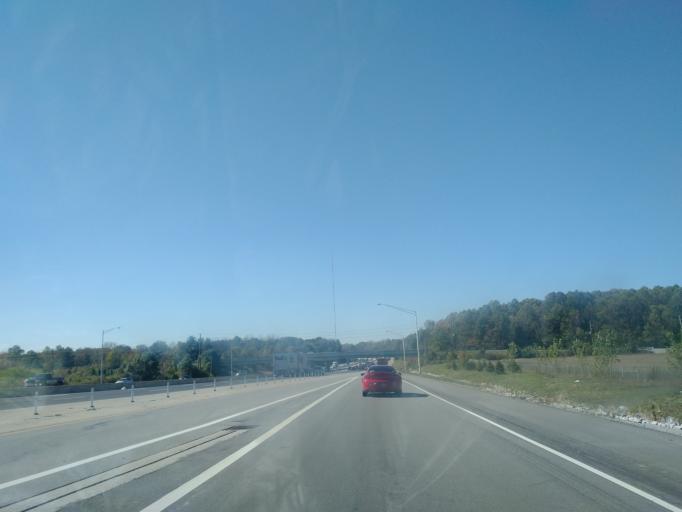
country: US
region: Indiana
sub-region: Marion County
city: Meridian Hills
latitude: 39.9305
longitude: -86.1622
